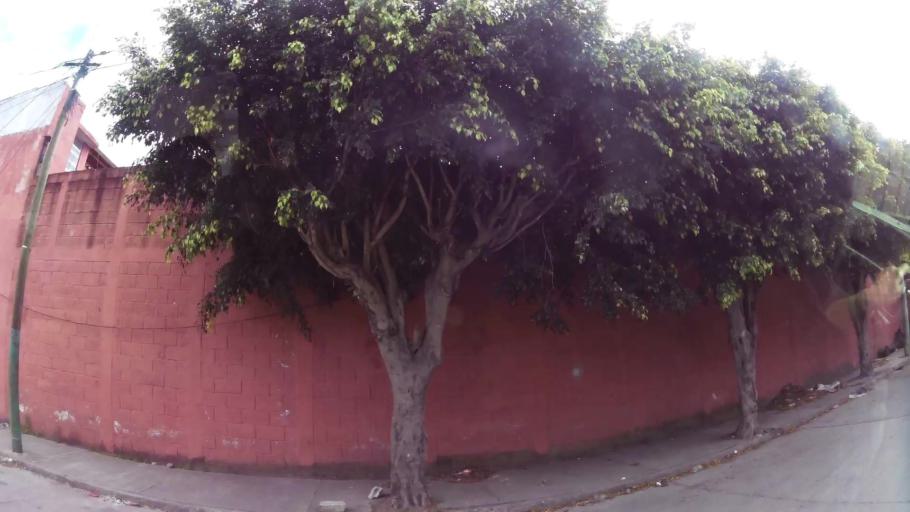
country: GT
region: Guatemala
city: Guatemala City
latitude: 14.6424
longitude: -90.5531
